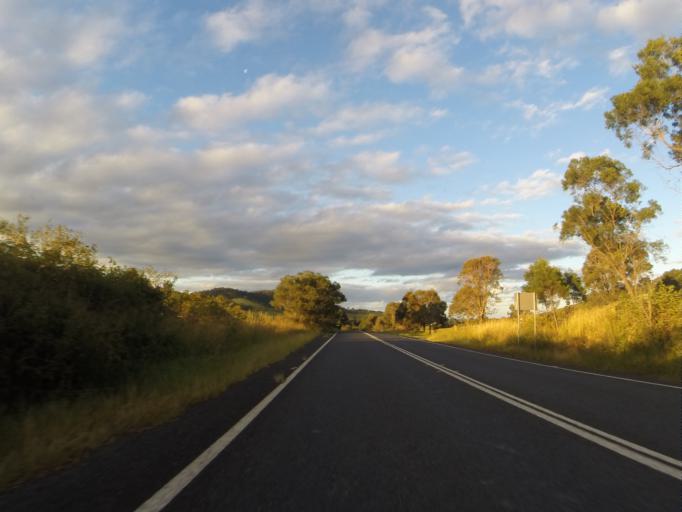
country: AU
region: New South Wales
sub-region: Shellharbour
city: Calderwood
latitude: -34.5815
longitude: 150.7210
